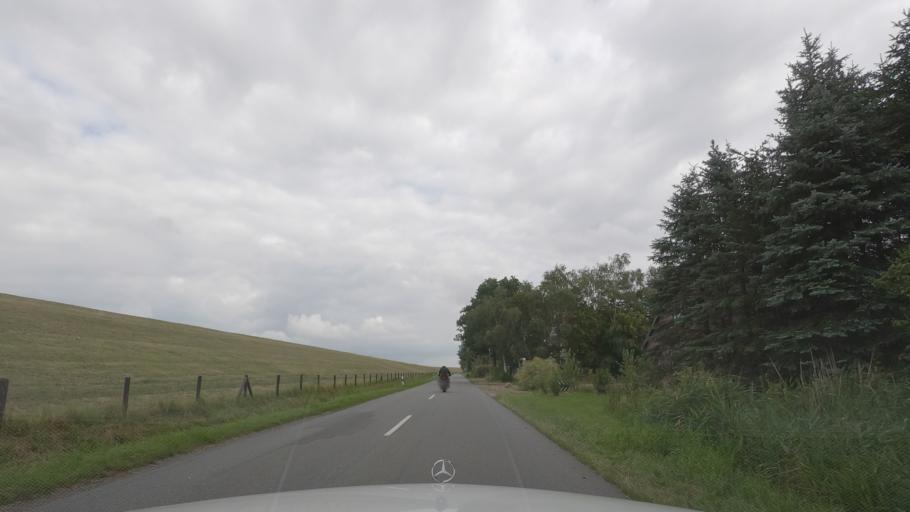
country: DE
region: Lower Saxony
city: Brake (Unterweser)
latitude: 53.3008
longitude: 8.5281
